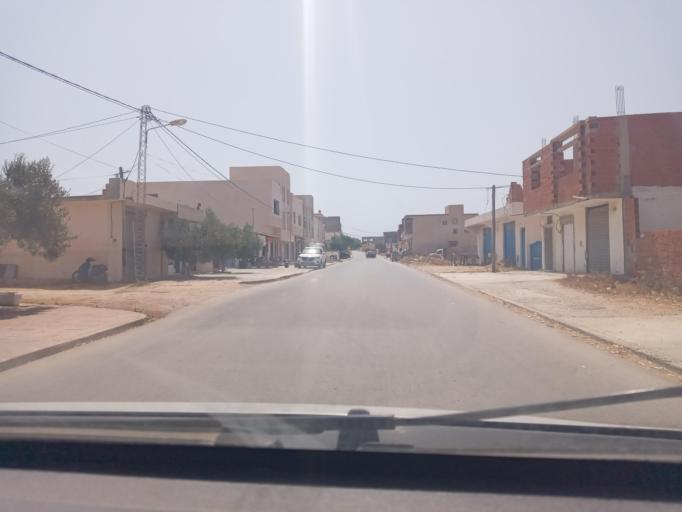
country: TN
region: Nabul
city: El Haouaria
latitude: 37.0456
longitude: 11.0219
